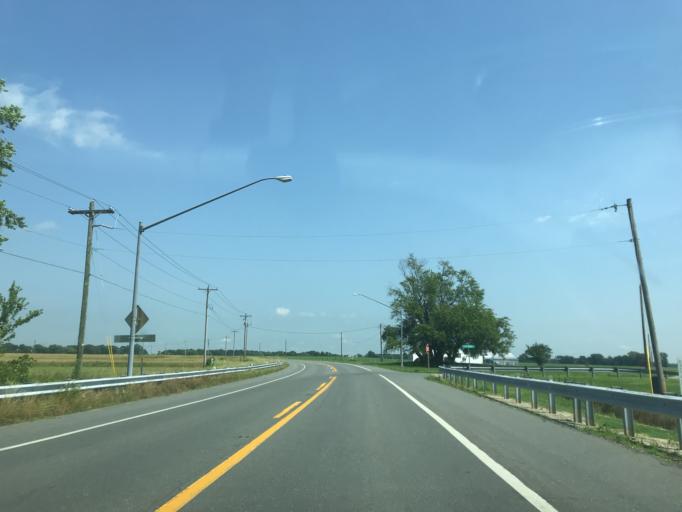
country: US
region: Maryland
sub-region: Dorchester County
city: Hurlock
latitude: 38.5940
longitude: -75.8945
